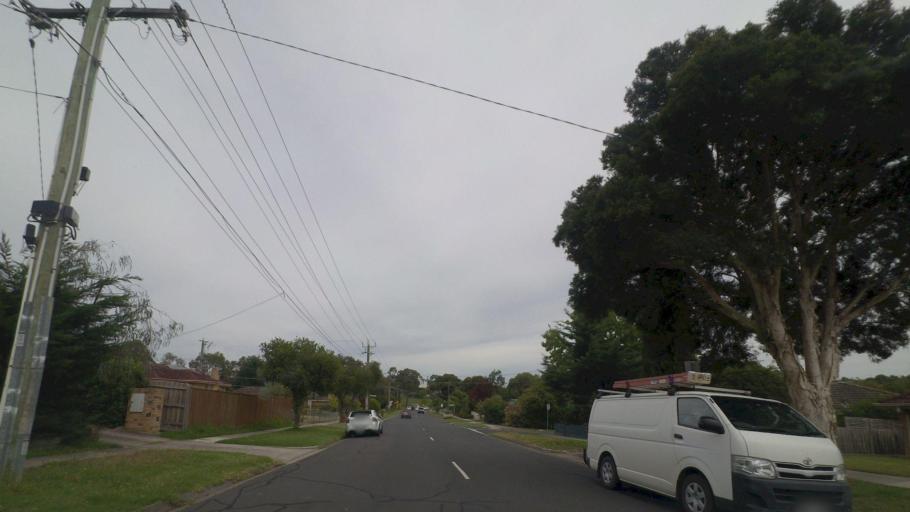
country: AU
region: Victoria
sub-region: Yarra Ranges
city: Kilsyth
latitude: -37.7884
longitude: 145.3217
